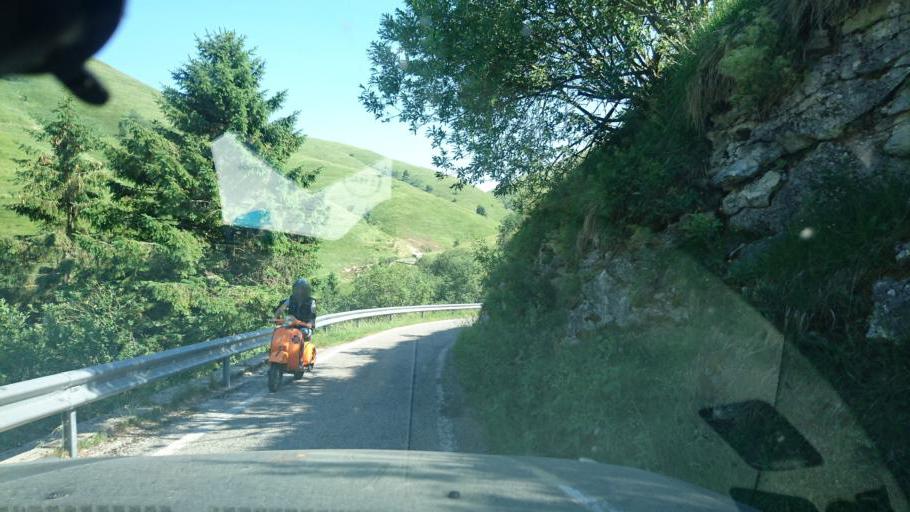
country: IT
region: Veneto
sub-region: Provincia di Treviso
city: Crespano del Grappa
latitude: 45.8885
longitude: 11.8355
